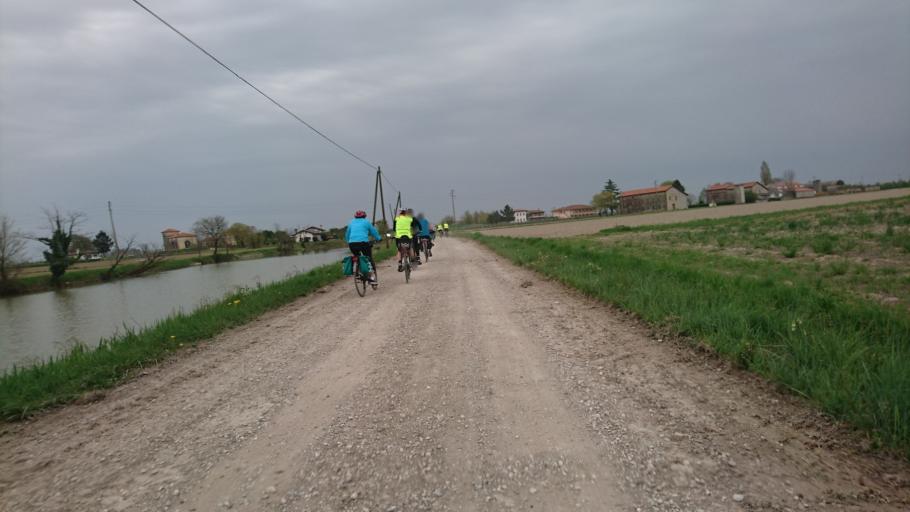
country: IT
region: Veneto
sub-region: Provincia di Venezia
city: Lugugnana
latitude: 45.6870
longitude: 12.9442
